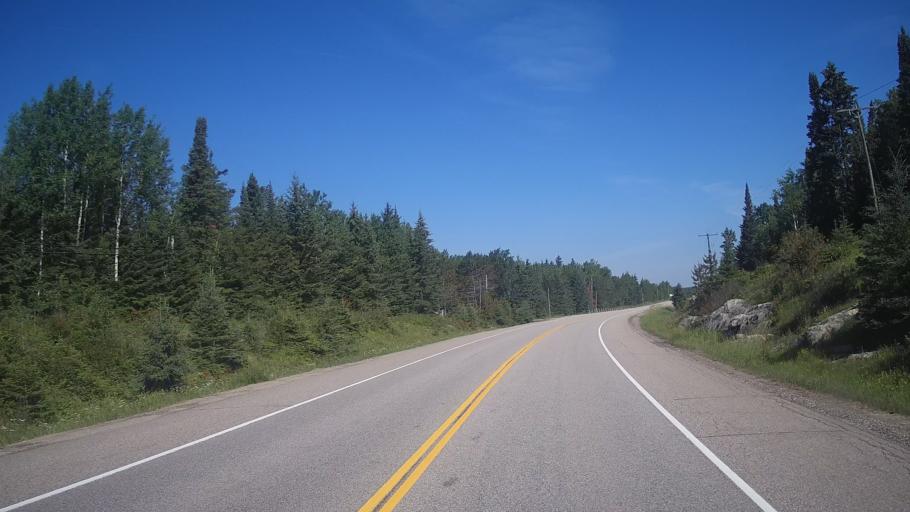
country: CA
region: Ontario
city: Dryden
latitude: 49.7692
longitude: -92.6885
